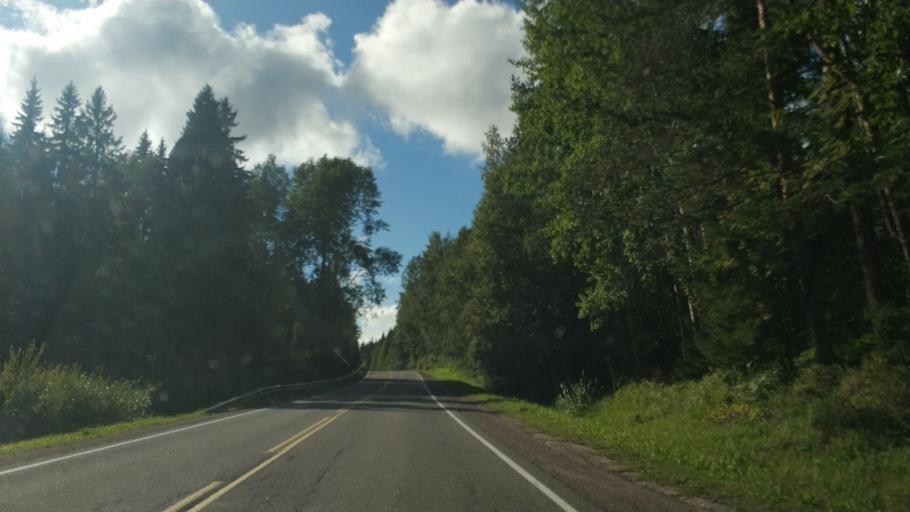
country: RU
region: Republic of Karelia
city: Sortavala
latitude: 61.6565
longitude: 30.6444
